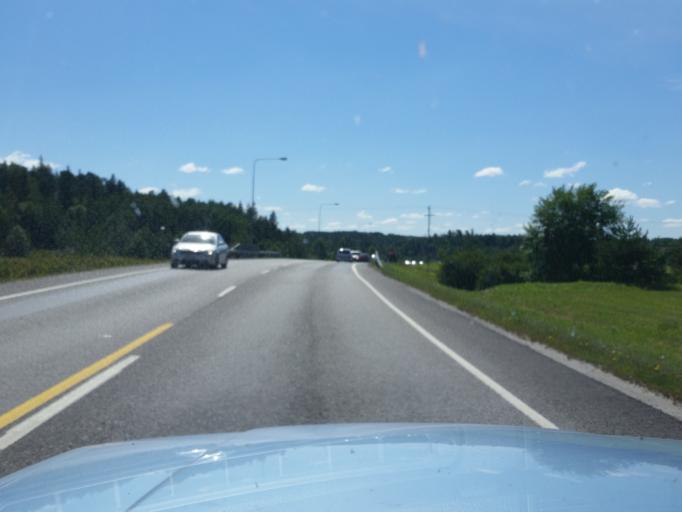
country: FI
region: Varsinais-Suomi
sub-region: Turku
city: Kaarina
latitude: 60.4057
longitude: 22.3876
